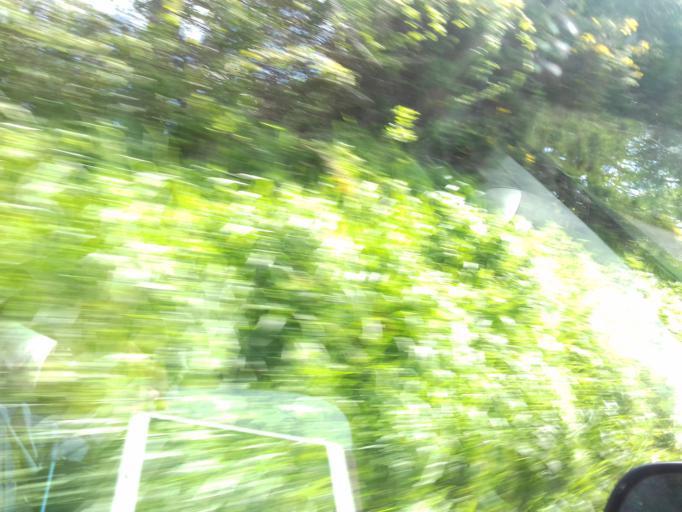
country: IE
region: Leinster
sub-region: Loch Garman
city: Castlebridge
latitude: 52.3924
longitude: -6.3877
